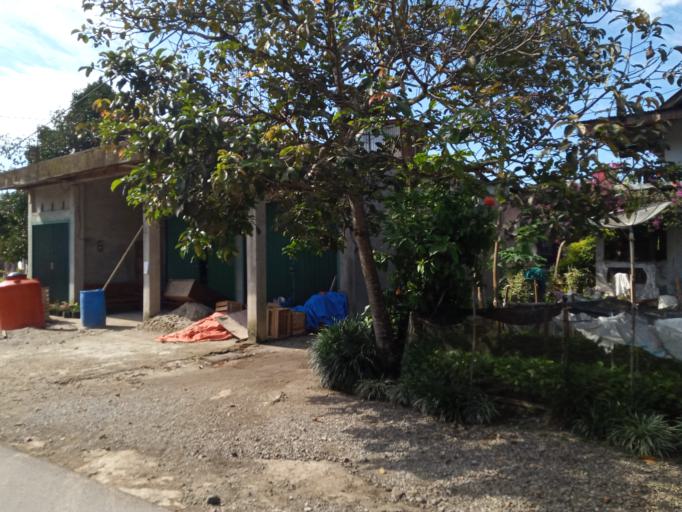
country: ID
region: Jambi
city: Sungai Penuh
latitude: -2.1627
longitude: 101.5888
